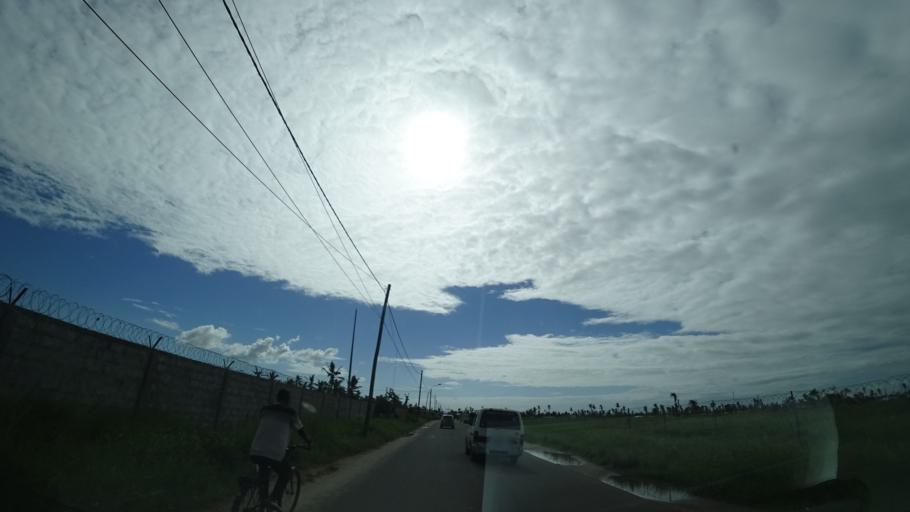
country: MZ
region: Sofala
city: Beira
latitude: -19.7938
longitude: 34.8903
